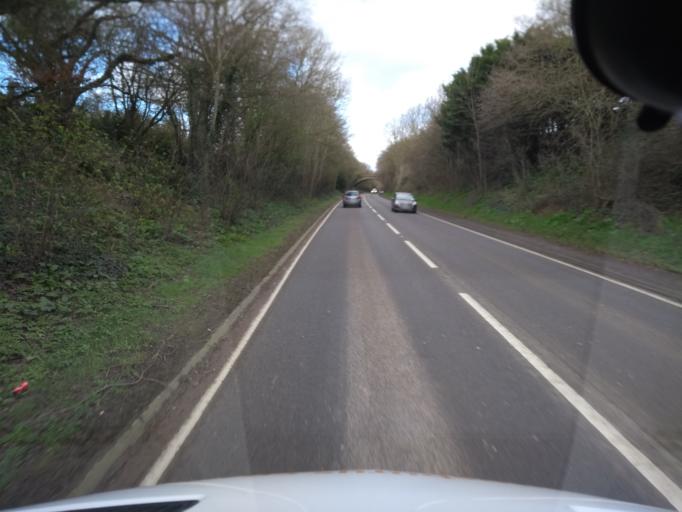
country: GB
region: England
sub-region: Somerset
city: Yeovil
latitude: 50.9418
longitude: -2.6803
